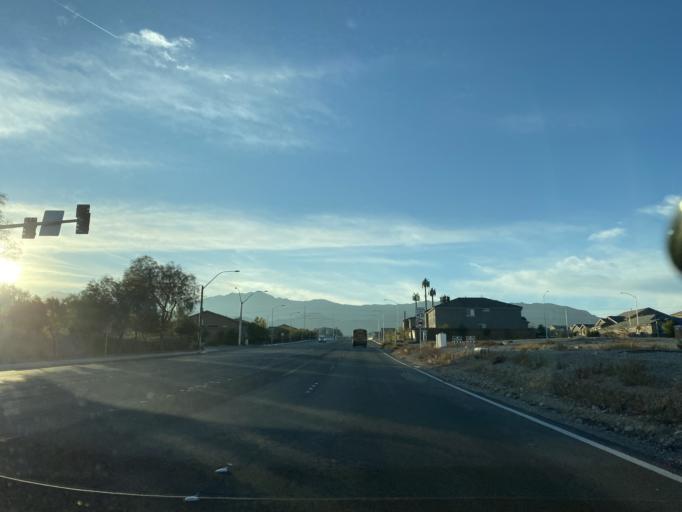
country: US
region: Nevada
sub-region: Clark County
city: Summerlin South
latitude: 36.2773
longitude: -115.3232
